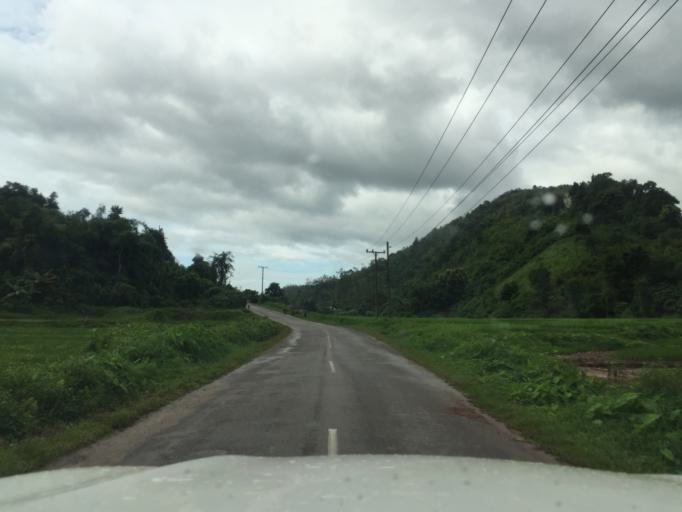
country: LA
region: Oudomxai
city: Muang La
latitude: 20.8190
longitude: 102.0936
